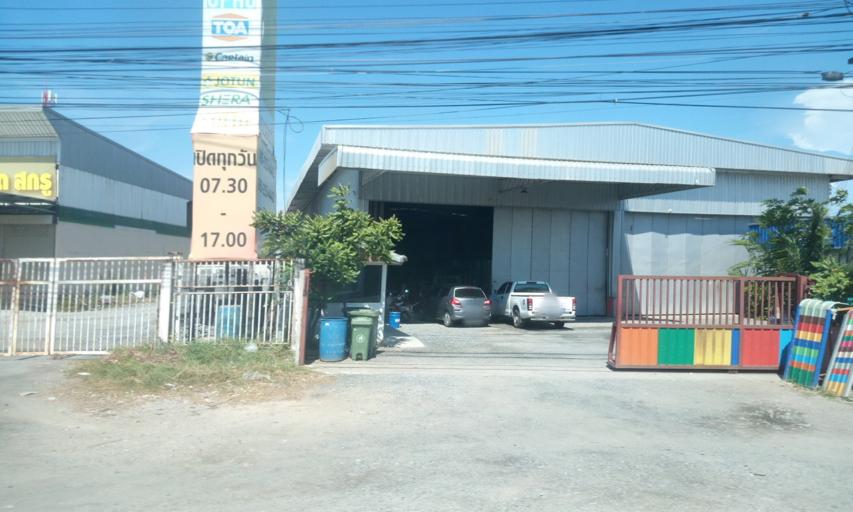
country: TH
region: Samut Prakan
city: Bang Bo District
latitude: 13.5308
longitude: 100.7883
